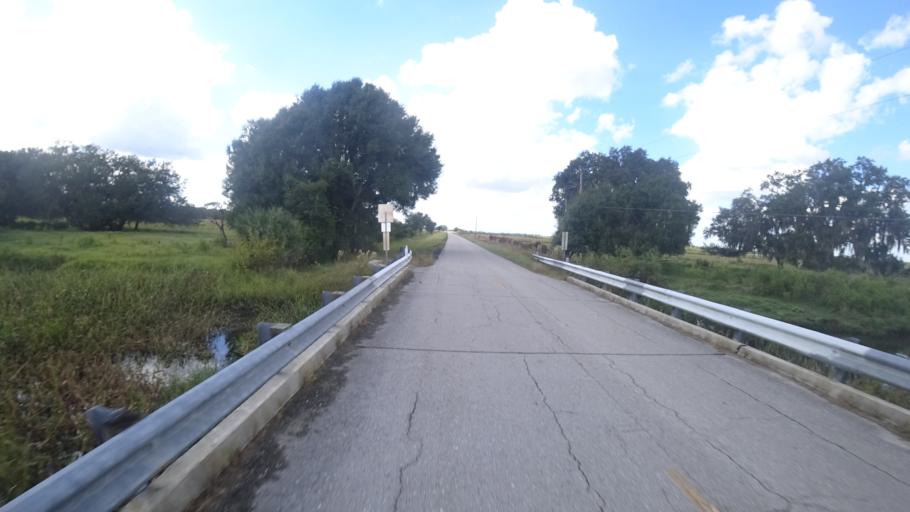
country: US
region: Florida
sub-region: Sarasota County
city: Warm Mineral Springs
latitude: 27.2737
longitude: -82.1631
